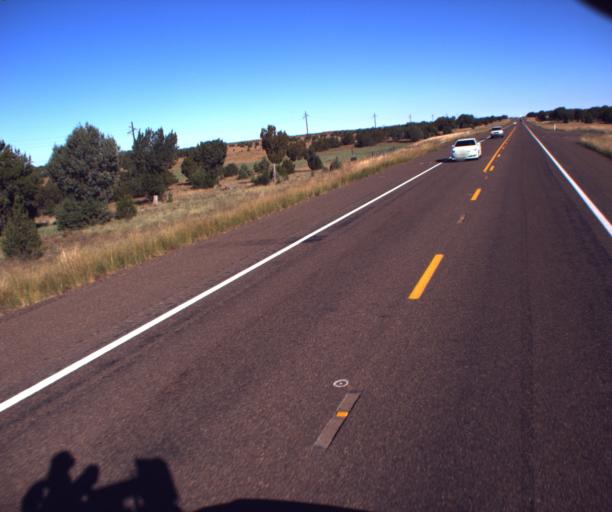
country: US
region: Arizona
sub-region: Navajo County
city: Show Low
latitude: 34.2866
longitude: -110.0295
